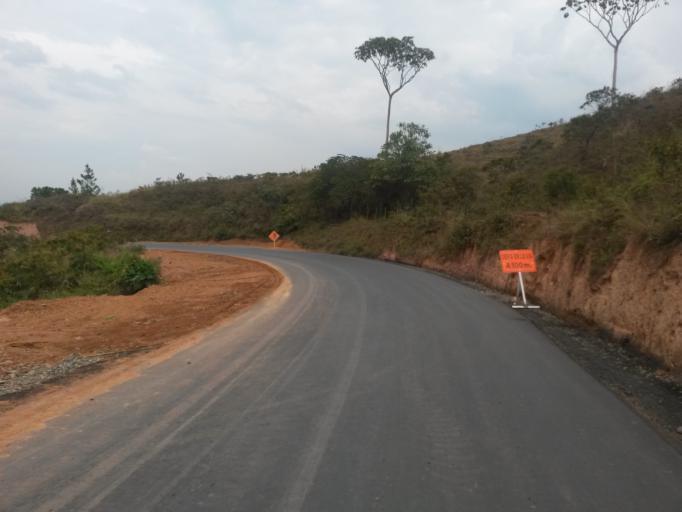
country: CO
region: Cauca
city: Buenos Aires
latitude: 3.0608
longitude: -76.6243
